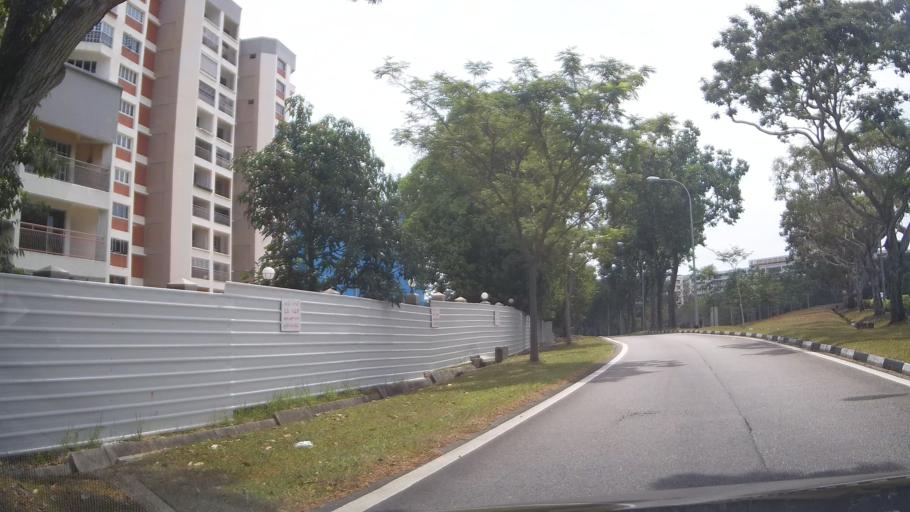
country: SG
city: Singapore
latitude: 1.3438
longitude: 103.9466
